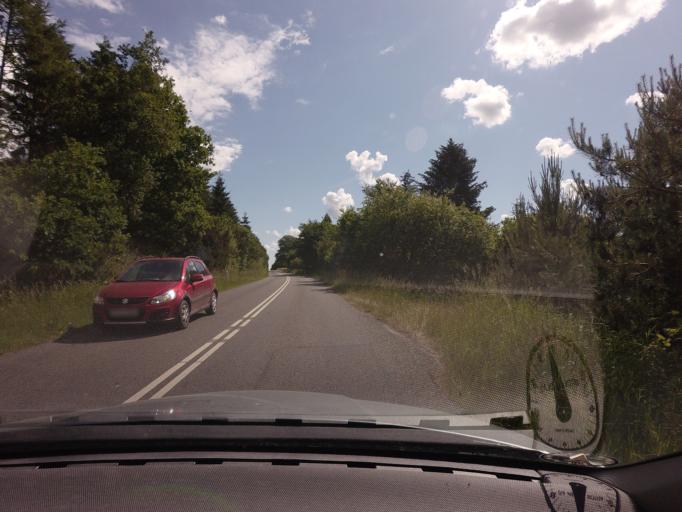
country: DK
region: Central Jutland
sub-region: Syddjurs Kommune
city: Ryomgard
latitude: 56.3555
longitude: 10.5154
